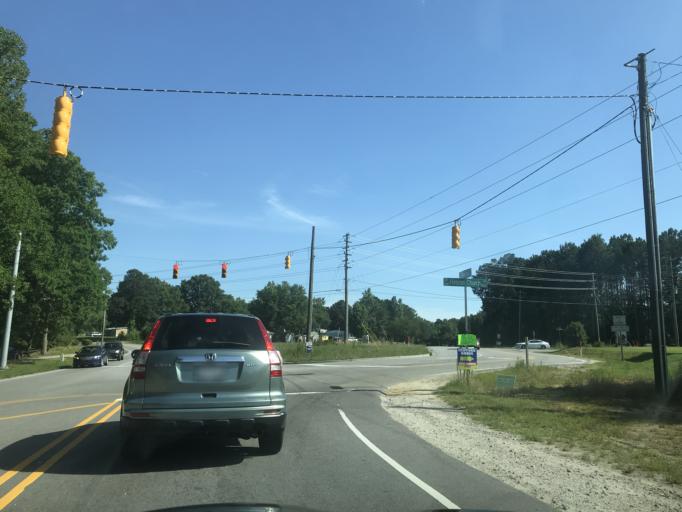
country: US
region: North Carolina
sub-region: Wake County
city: Garner
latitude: 35.6707
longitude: -78.5753
